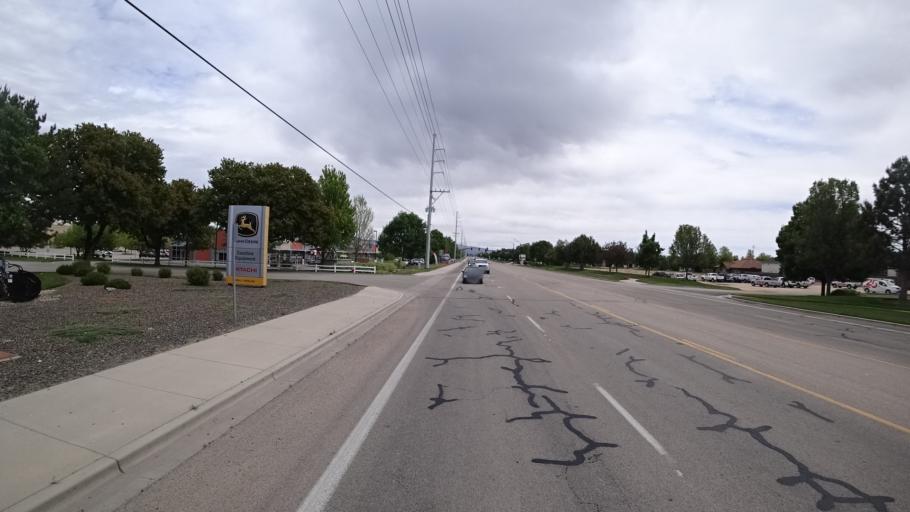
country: US
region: Idaho
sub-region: Ada County
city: Meridian
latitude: 43.5904
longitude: -116.3699
